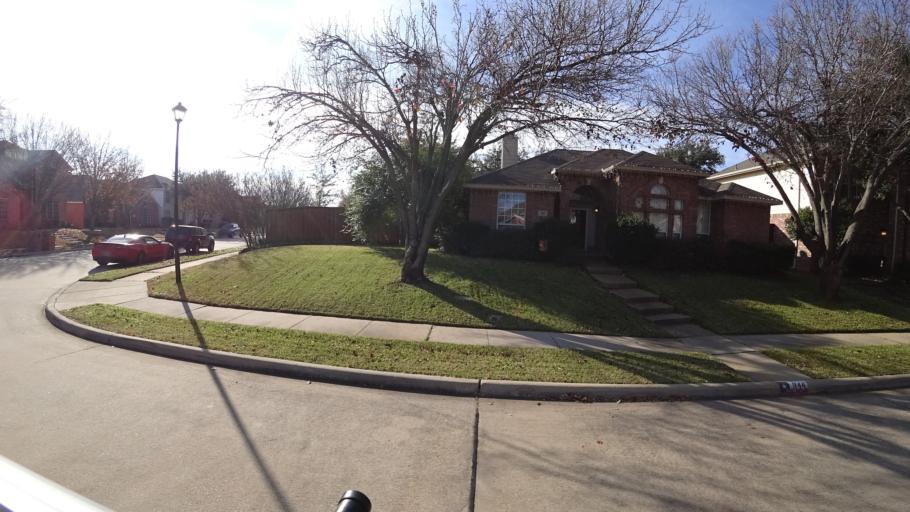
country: US
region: Texas
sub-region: Denton County
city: Lewisville
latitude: 33.0534
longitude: -97.0198
